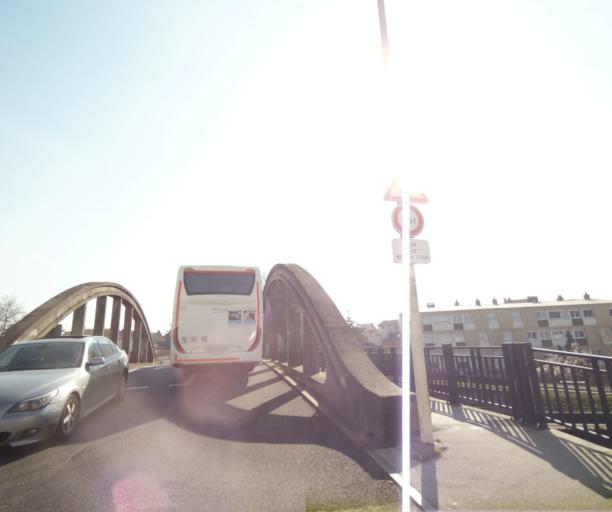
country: FR
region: Lorraine
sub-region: Departement de Meurthe-et-Moselle
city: Maxeville
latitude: 48.7044
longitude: 6.1746
